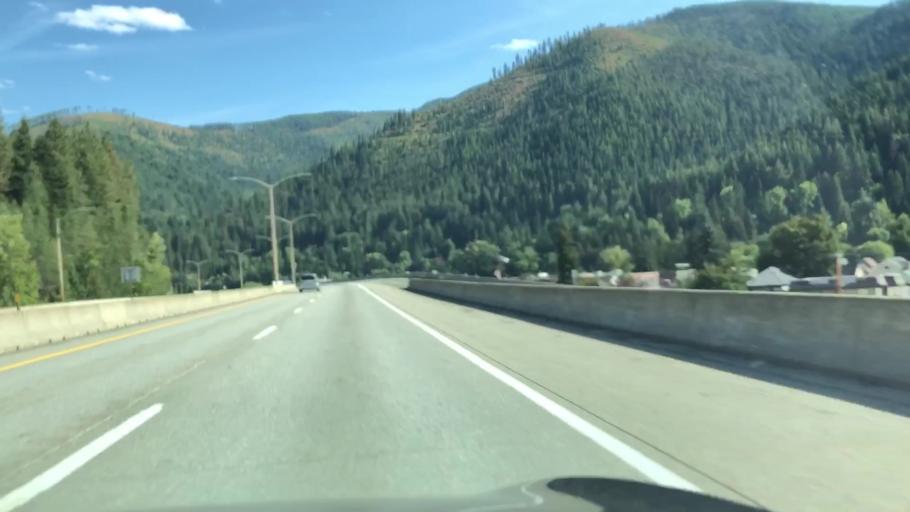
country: US
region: Idaho
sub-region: Shoshone County
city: Wallace
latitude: 47.4765
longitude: -115.9301
